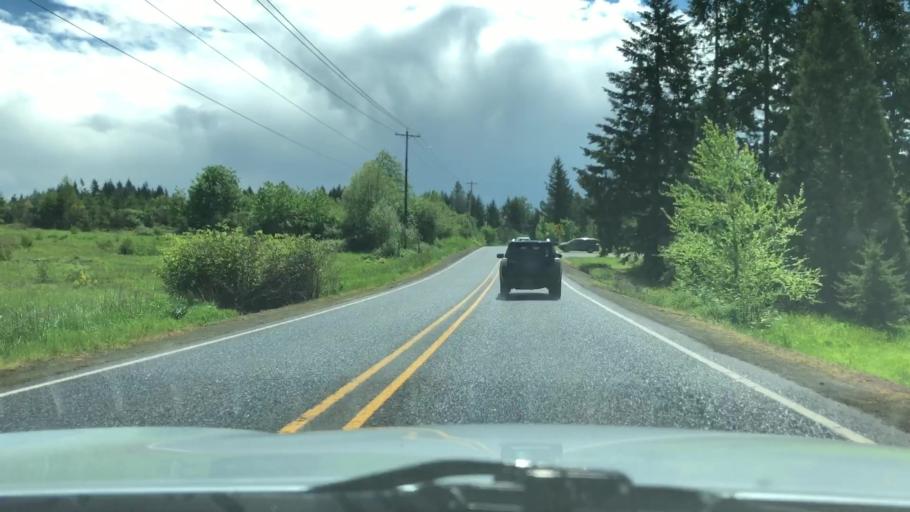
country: US
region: Oregon
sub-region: Clackamas County
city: Beavercreek
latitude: 45.3043
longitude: -122.5436
